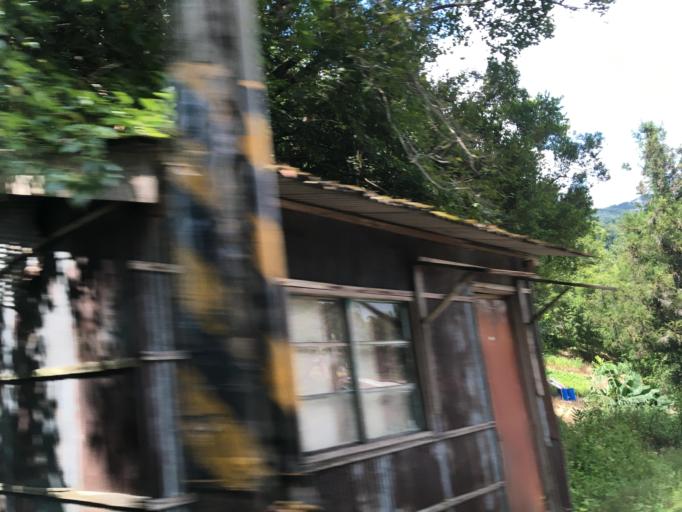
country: TW
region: Taiwan
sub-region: Yilan
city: Yilan
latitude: 24.9325
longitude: 121.6891
